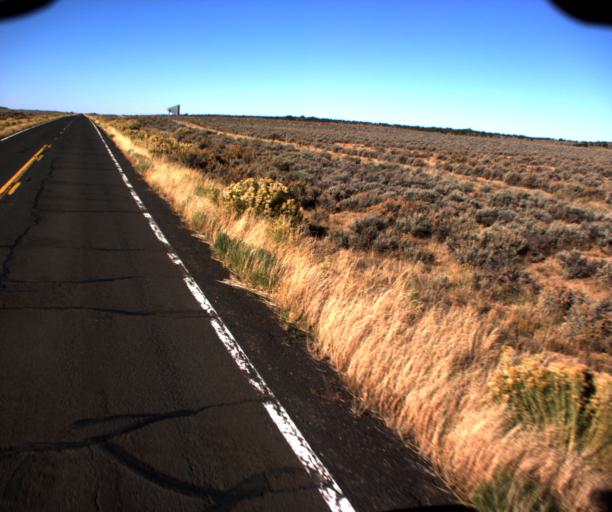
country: US
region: Arizona
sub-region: Navajo County
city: First Mesa
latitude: 35.7612
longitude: -110.0066
